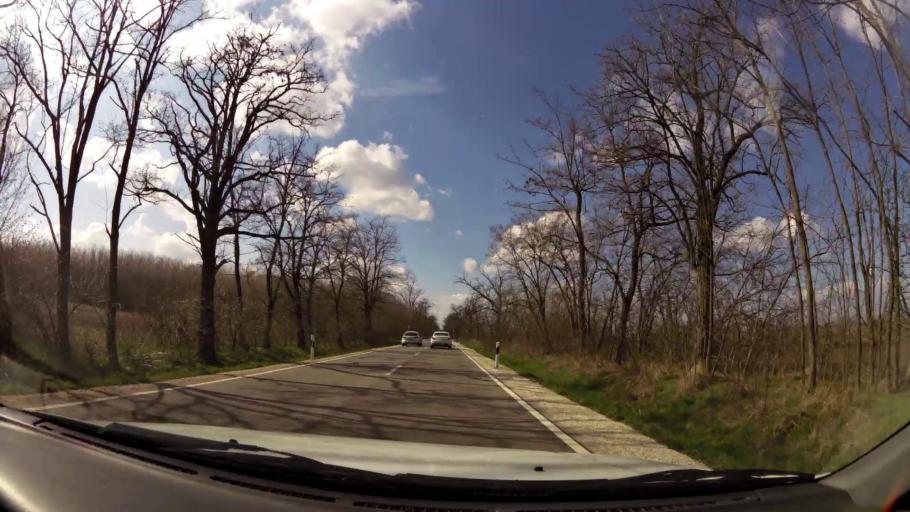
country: HU
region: Pest
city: Forropuszta
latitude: 47.4588
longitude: 19.6624
